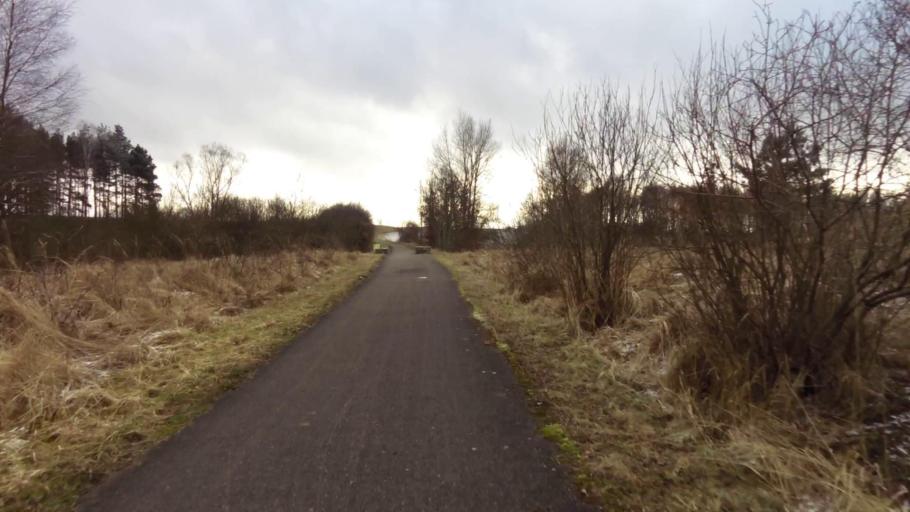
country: PL
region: West Pomeranian Voivodeship
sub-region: Powiat drawski
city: Zlocieniec
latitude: 53.6022
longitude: 16.0457
